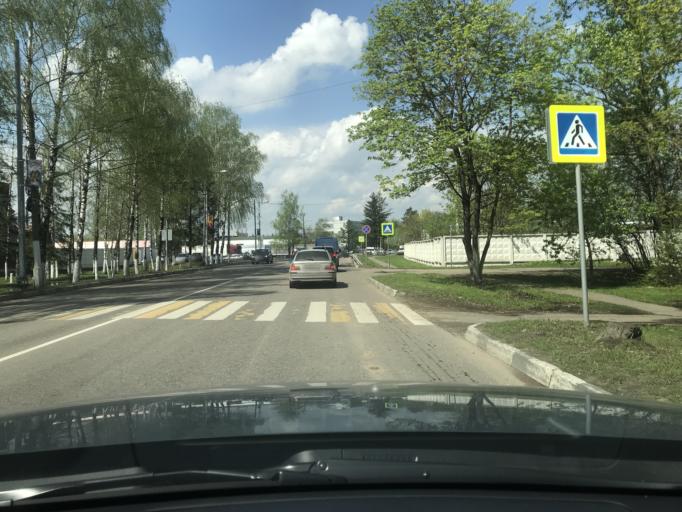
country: RU
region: Moskovskaya
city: Naro-Fominsk
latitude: 55.3765
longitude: 36.7643
